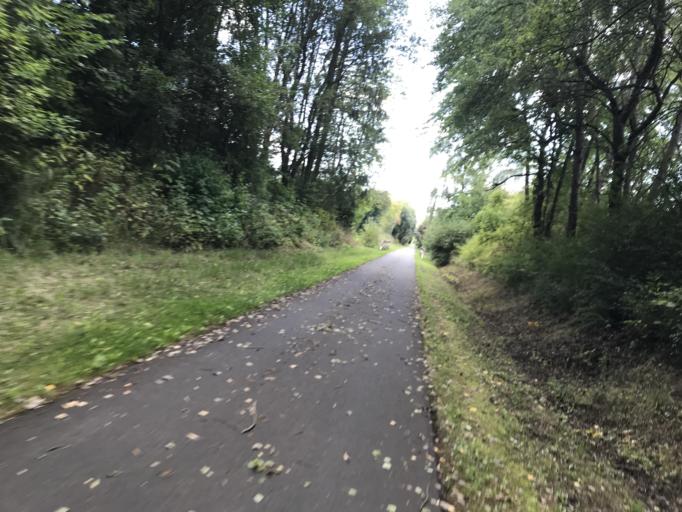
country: DE
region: Hesse
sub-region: Regierungsbezirk Kassel
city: Sachsenhausen
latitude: 51.2496
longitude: 9.0051
